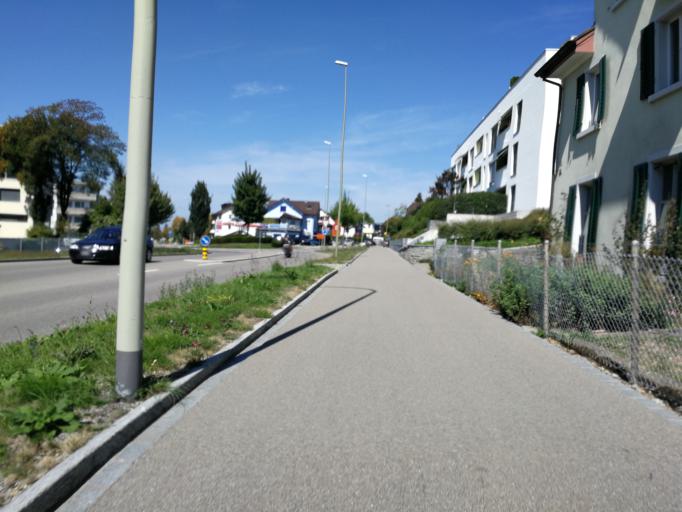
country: CH
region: Zurich
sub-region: Bezirk Hinwil
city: Hinwil
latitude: 47.2961
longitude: 8.8406
